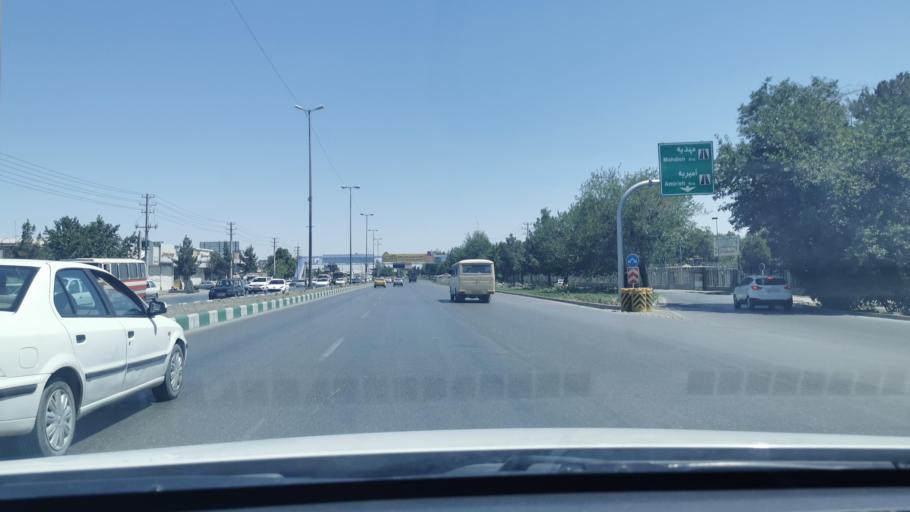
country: IR
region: Razavi Khorasan
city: Mashhad
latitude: 36.4042
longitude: 59.4794
